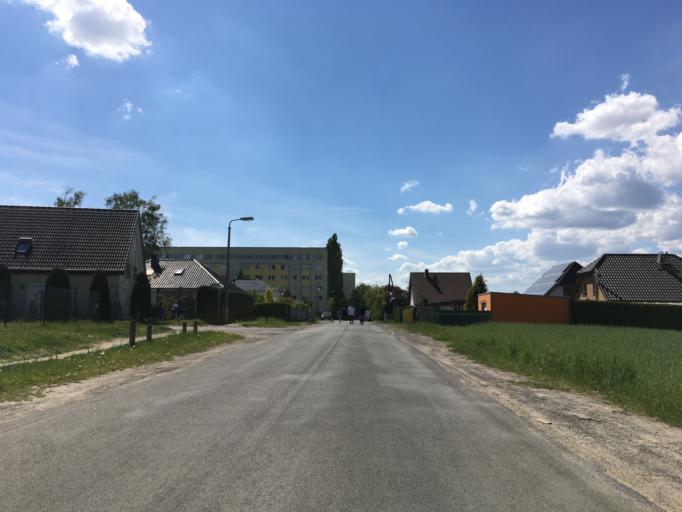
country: DE
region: Brandenburg
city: Bernau bei Berlin
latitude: 52.6725
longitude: 13.5615
